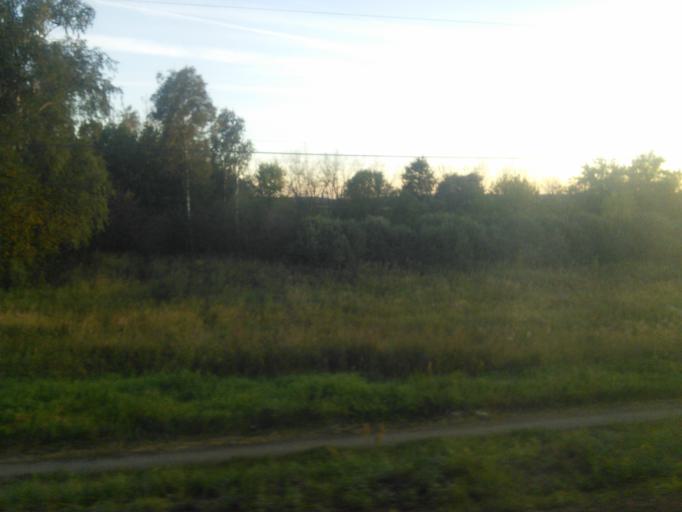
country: RU
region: Moskovskaya
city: Elektrougli
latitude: 55.7373
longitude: 38.1765
